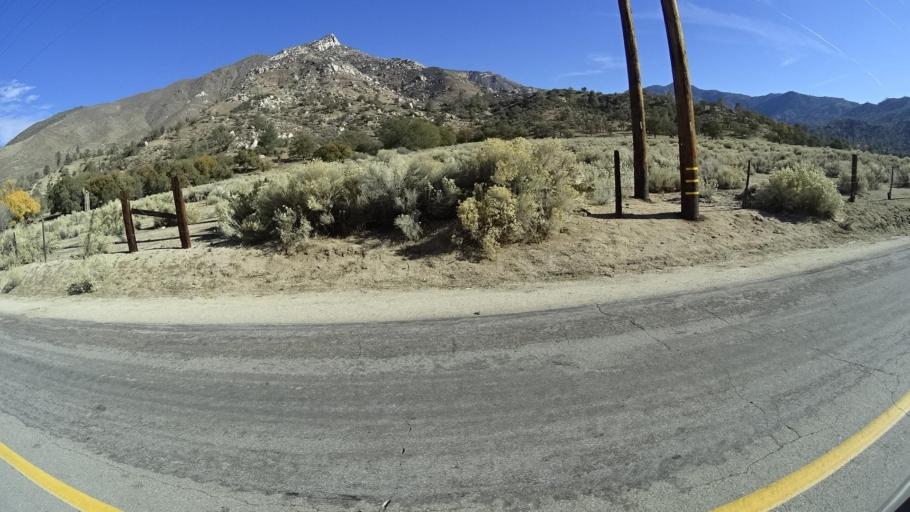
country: US
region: California
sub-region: Kern County
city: Bodfish
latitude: 35.5425
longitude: -118.5096
